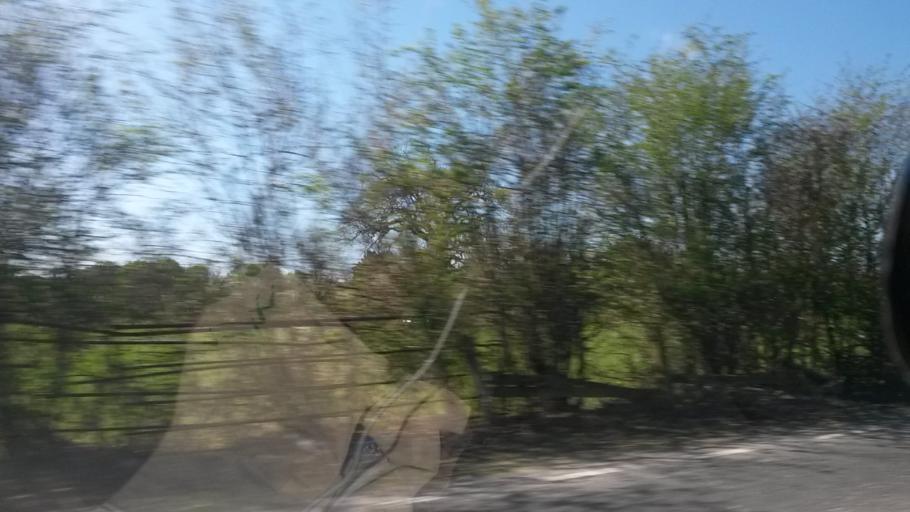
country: IE
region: Munster
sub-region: County Cork
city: Blarney
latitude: 51.8955
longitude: -8.5364
